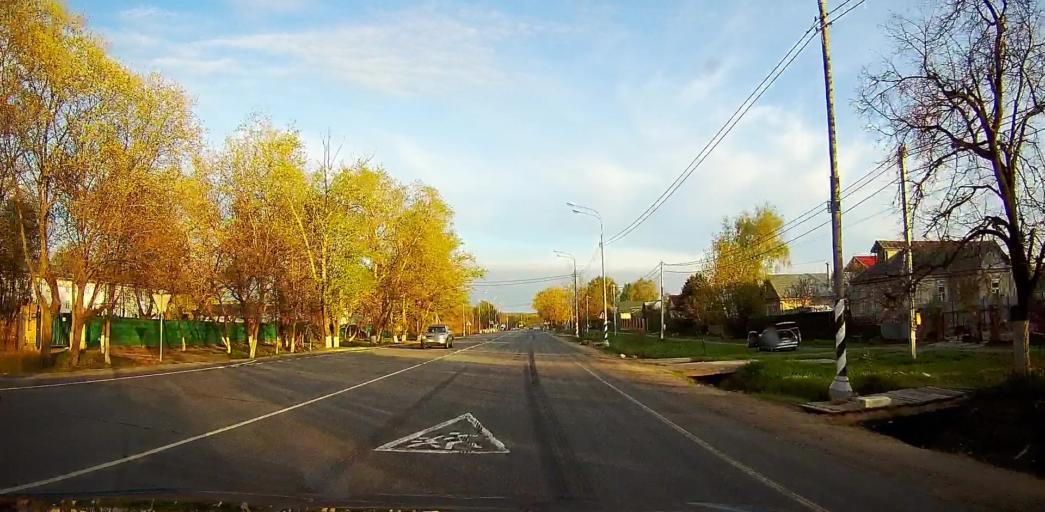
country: RU
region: Moskovskaya
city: Troitskoye
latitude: 55.2085
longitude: 38.6075
